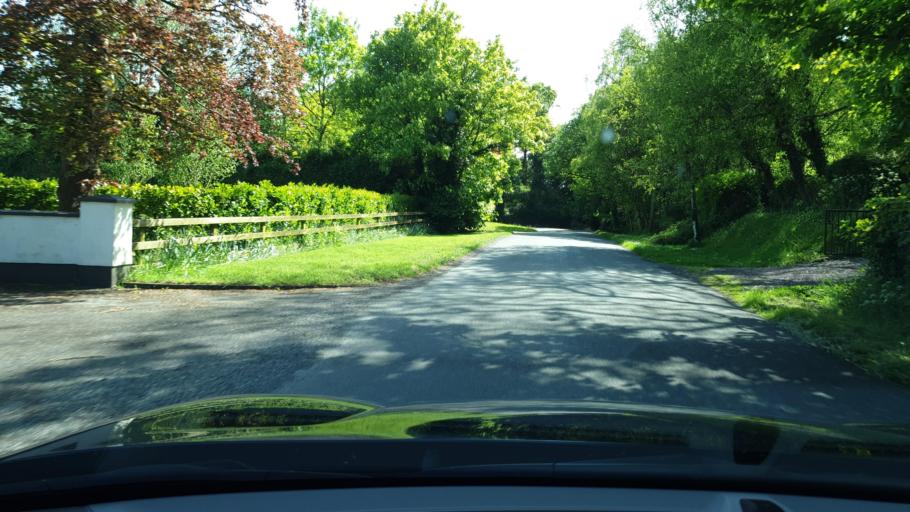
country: IE
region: Leinster
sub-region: An Mhi
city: Dunshaughlin
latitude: 53.4799
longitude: -6.5384
